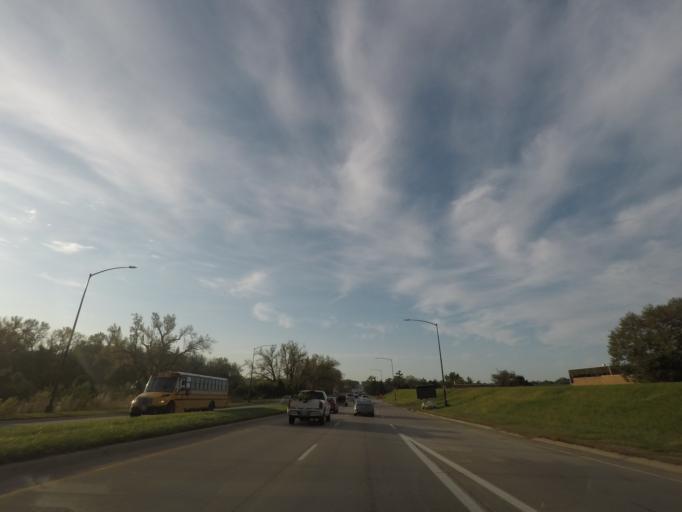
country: US
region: Iowa
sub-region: Polk County
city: Des Moines
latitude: 41.5782
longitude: -93.6450
